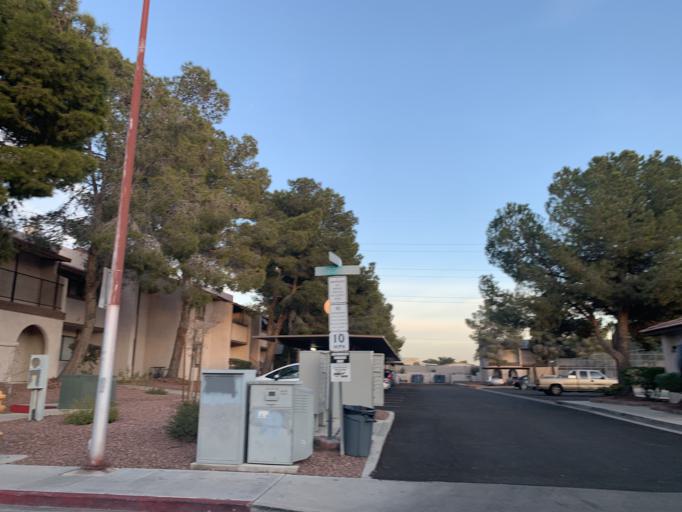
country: US
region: Nevada
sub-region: Clark County
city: Spring Valley
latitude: 36.1067
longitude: -115.2138
